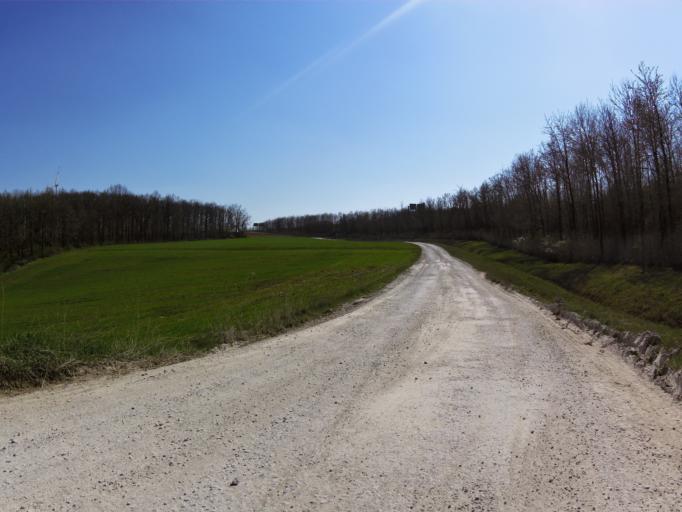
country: DE
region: Bavaria
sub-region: Regierungsbezirk Unterfranken
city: Biebelried
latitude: 49.7775
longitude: 10.0958
